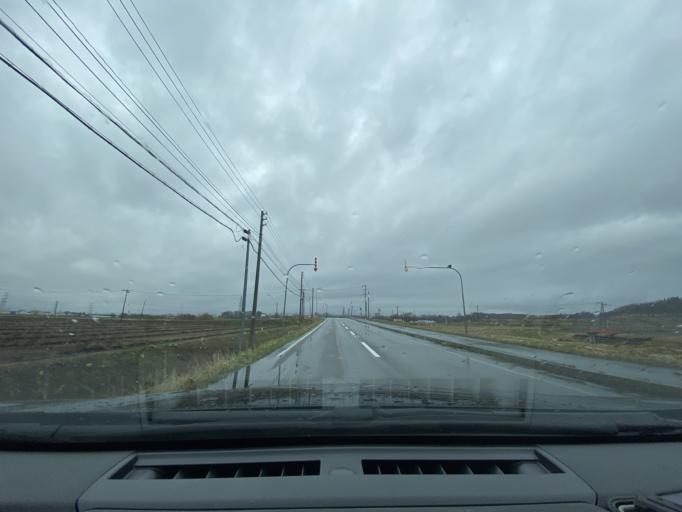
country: JP
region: Hokkaido
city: Fukagawa
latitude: 43.8133
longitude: 141.9607
